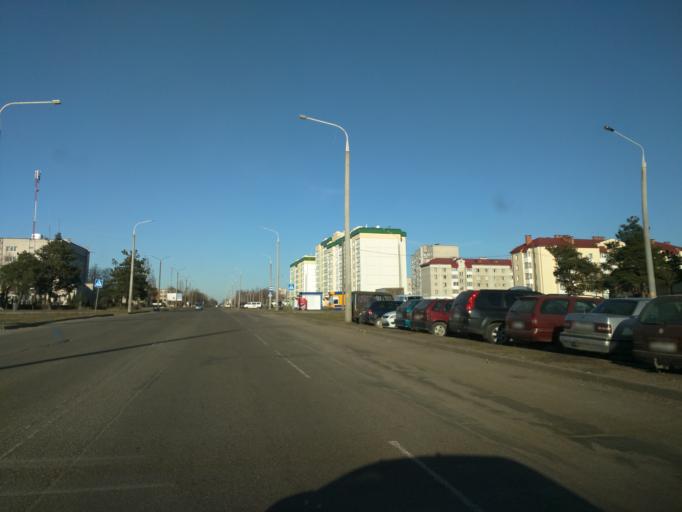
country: BY
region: Mogilev
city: Babruysk
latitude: 53.1684
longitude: 29.1664
